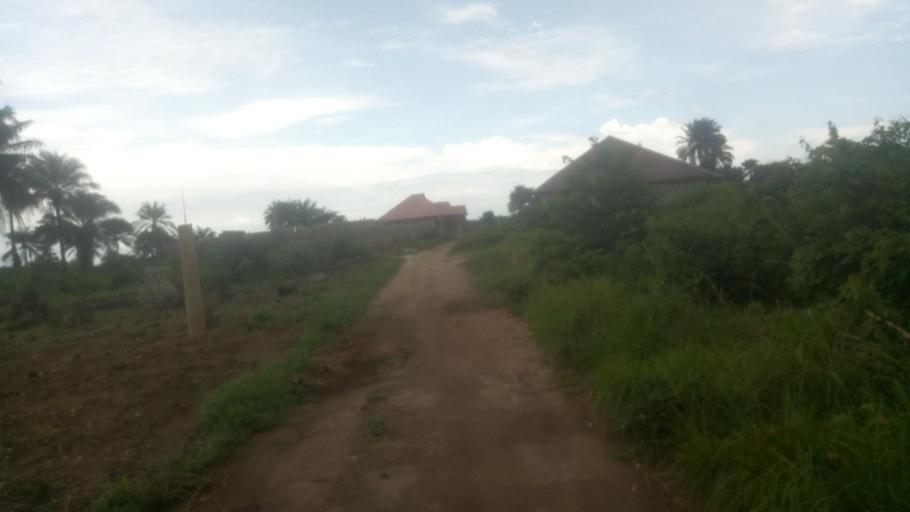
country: SL
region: Northern Province
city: Masoyila
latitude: 8.5735
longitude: -13.1660
